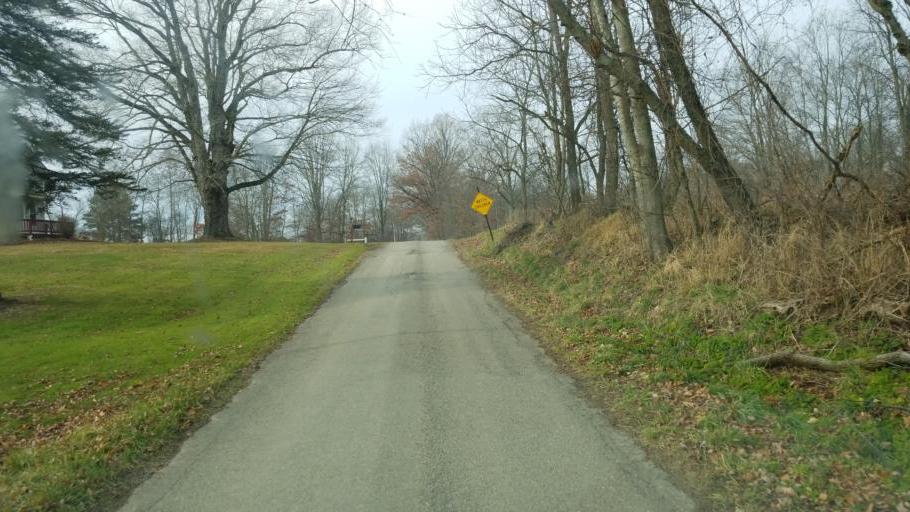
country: US
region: Pennsylvania
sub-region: Crawford County
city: Cochranton
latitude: 41.5201
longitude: -80.1169
